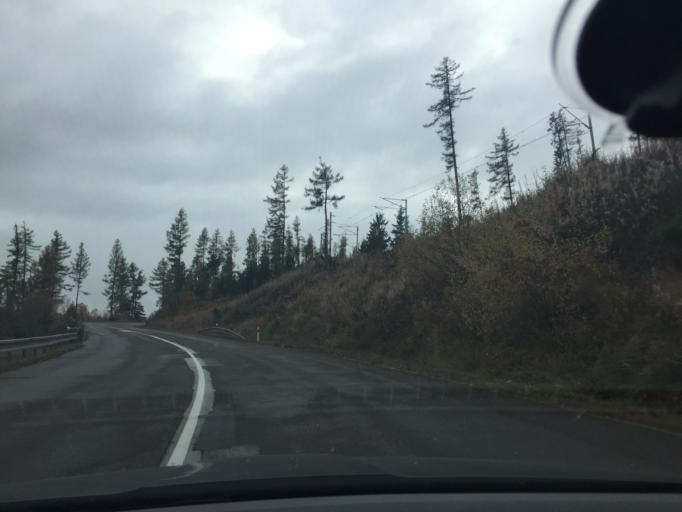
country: SK
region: Presovsky
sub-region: Okres Poprad
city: Strba
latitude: 49.1161
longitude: 20.0952
